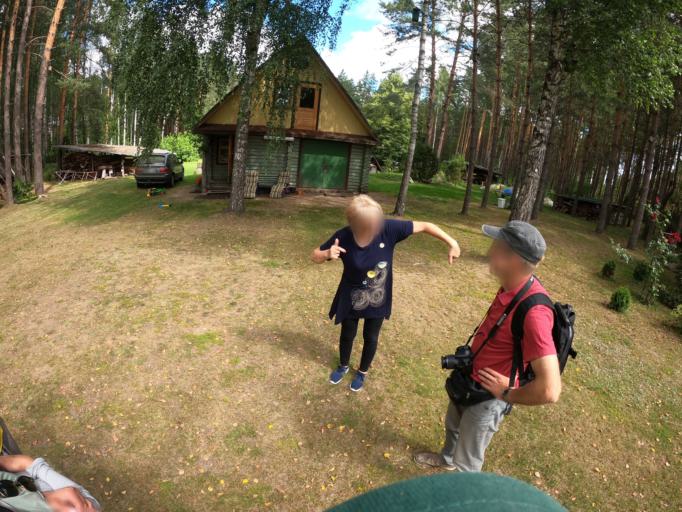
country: LT
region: Alytaus apskritis
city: Druskininkai
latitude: 54.1632
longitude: 24.1603
